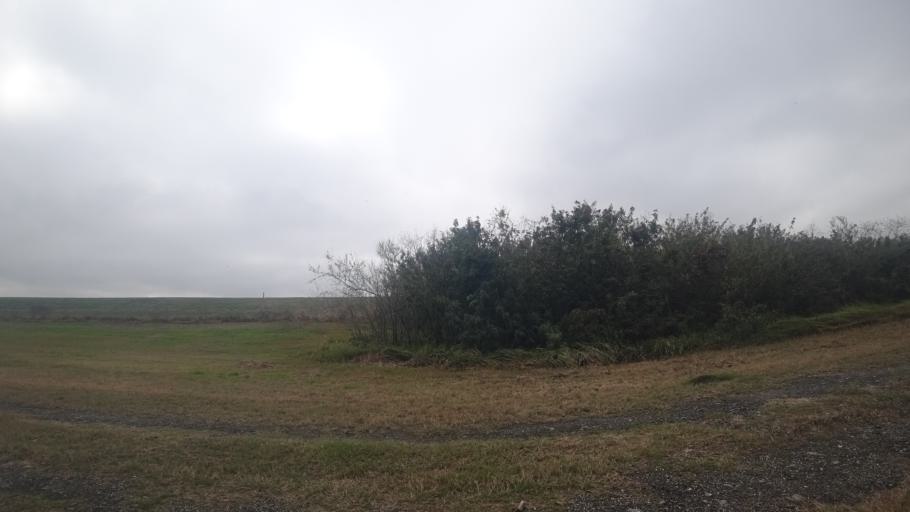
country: US
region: Florida
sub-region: Manatee County
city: Ellenton
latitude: 27.5906
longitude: -82.4853
